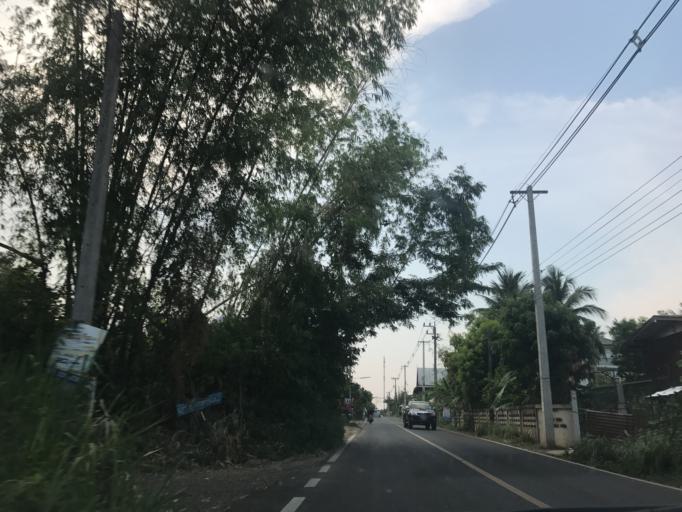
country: TH
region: Buriram
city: Nang Rong
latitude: 14.5827
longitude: 102.7910
